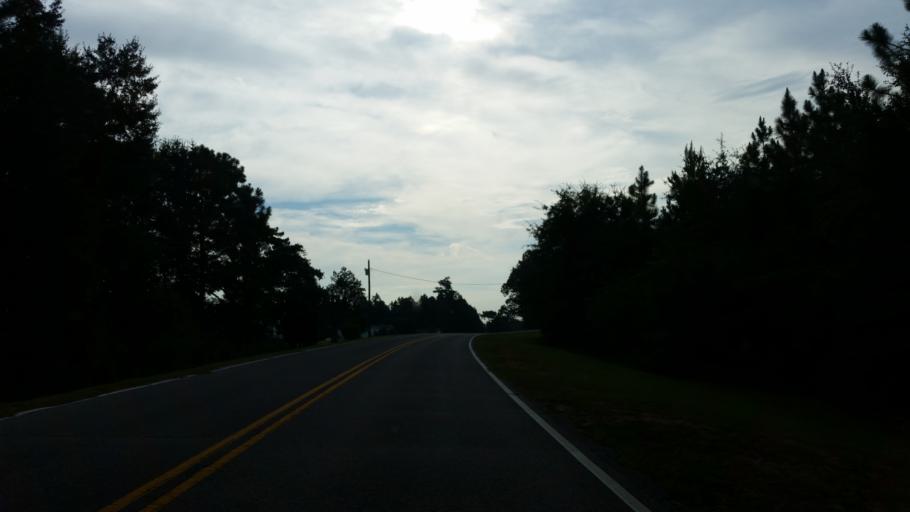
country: US
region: Florida
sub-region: Escambia County
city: Molino
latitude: 30.7739
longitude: -87.4848
